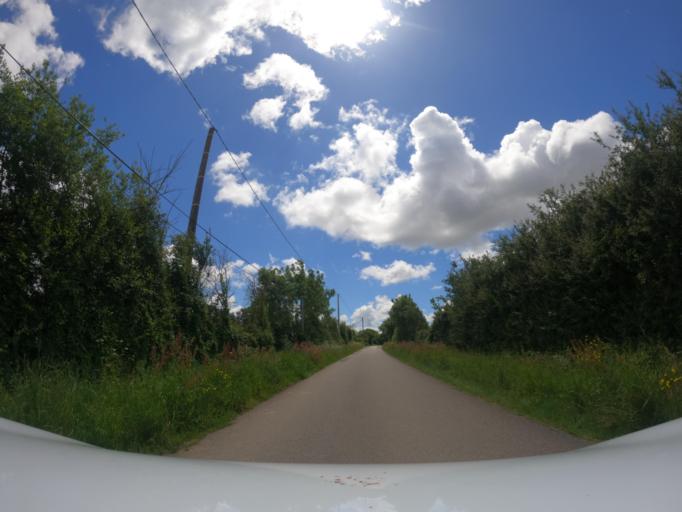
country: FR
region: Pays de la Loire
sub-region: Departement de la Vendee
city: Le Champ-Saint-Pere
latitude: 46.4910
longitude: -1.3571
